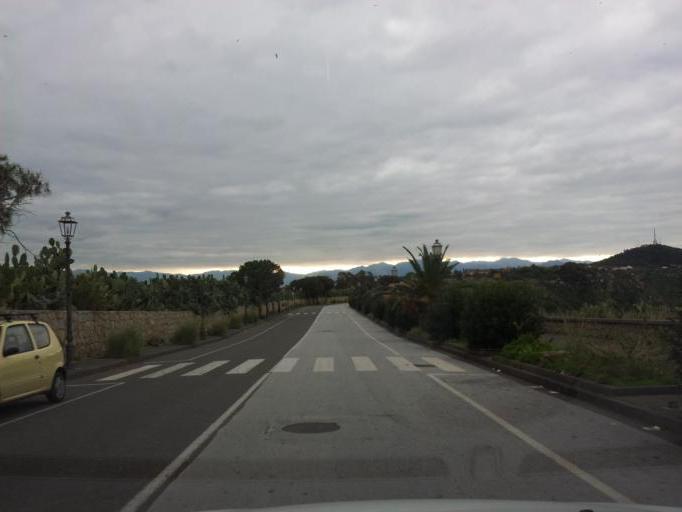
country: IT
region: Sicily
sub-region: Messina
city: Milazzo
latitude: 38.2675
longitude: 15.2358
